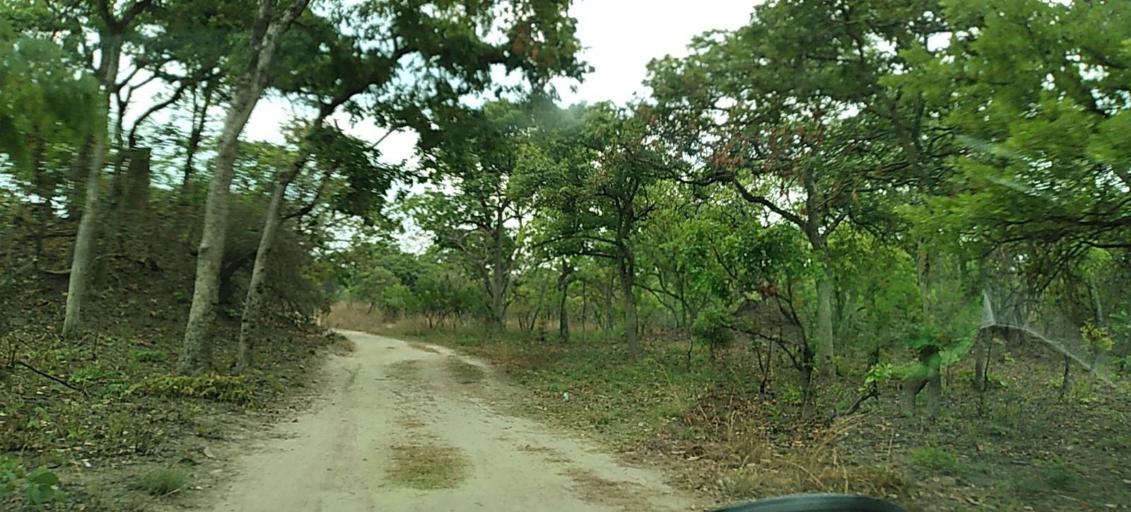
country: ZM
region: North-Western
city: Solwezi
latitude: -12.7878
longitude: 26.5238
